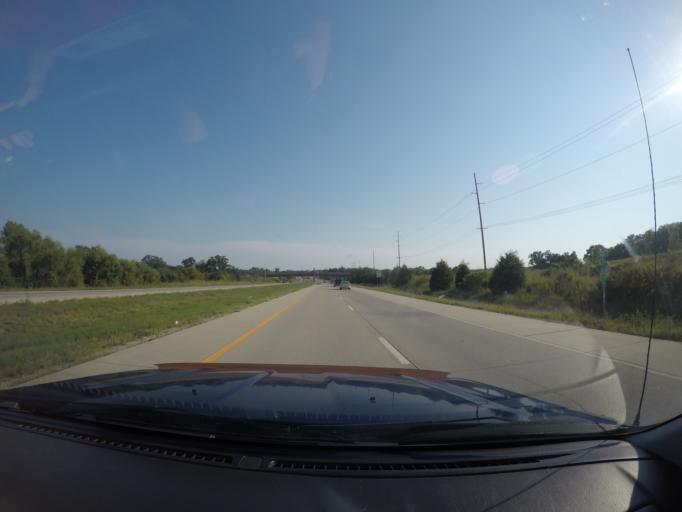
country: US
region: Kansas
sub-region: Wyandotte County
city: Bonner Springs
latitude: 39.0210
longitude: -94.8535
